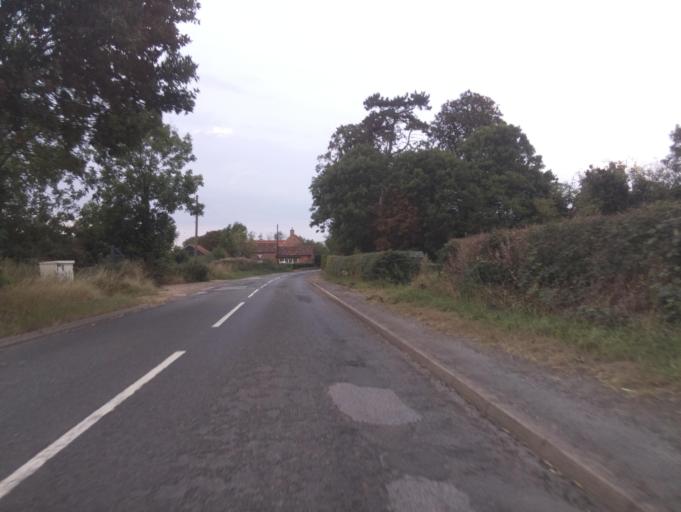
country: GB
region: England
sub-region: Lincolnshire
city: Skellingthorpe
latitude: 53.1412
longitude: -0.6458
